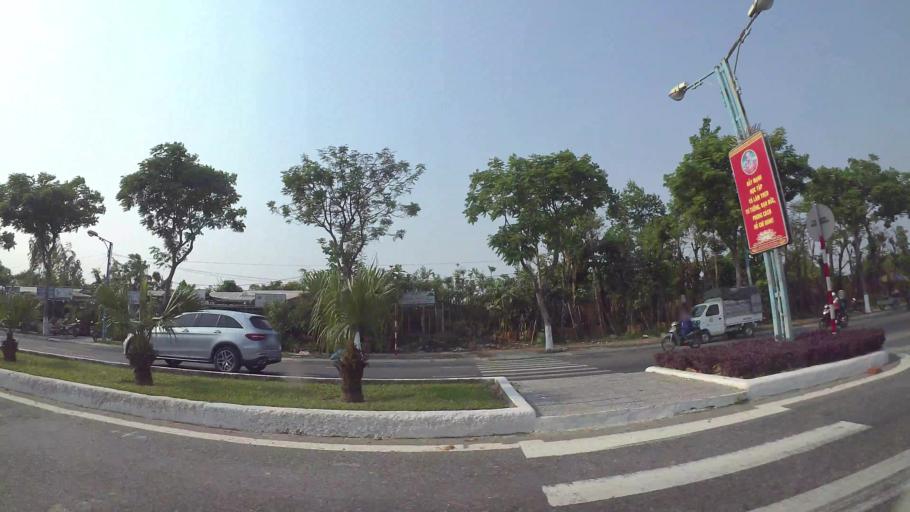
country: VN
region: Da Nang
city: Cam Le
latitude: 16.0237
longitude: 108.2057
